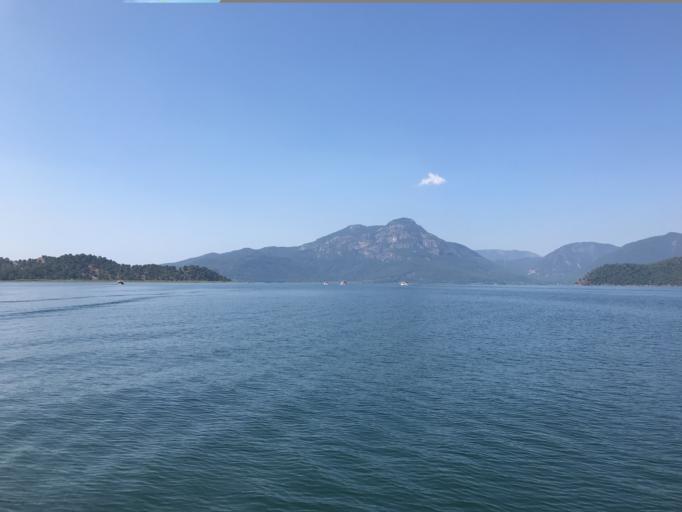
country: TR
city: Dalyan
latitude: 36.9109
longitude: 28.6532
